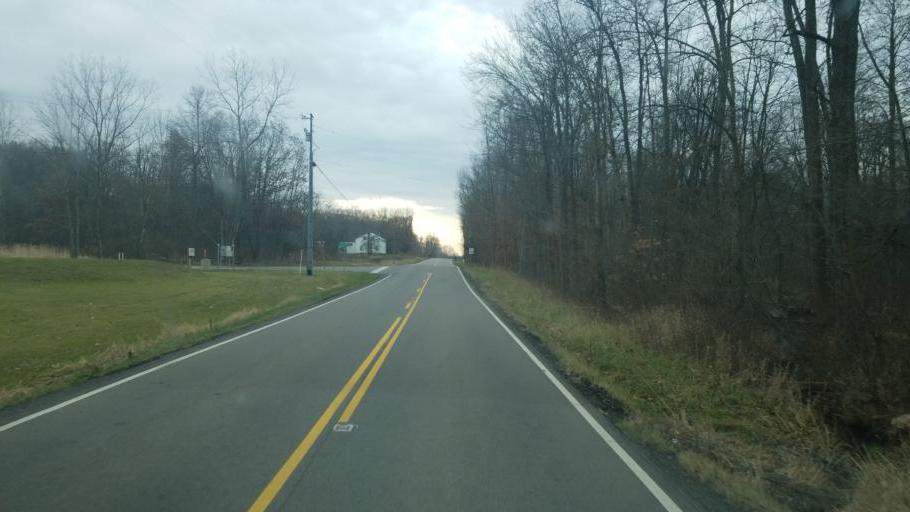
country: US
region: Ohio
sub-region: Knox County
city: Centerburg
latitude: 40.2992
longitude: -82.6400
